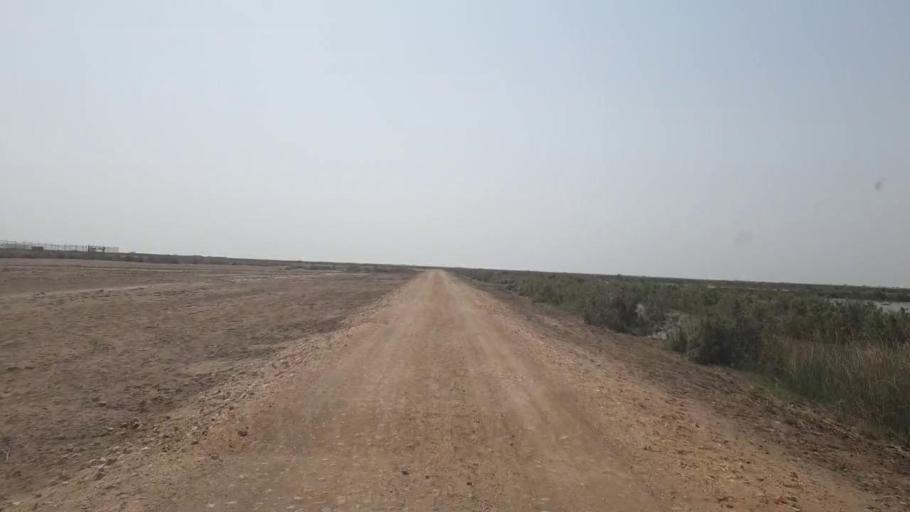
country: PK
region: Sindh
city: Jati
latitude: 24.3751
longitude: 68.6020
